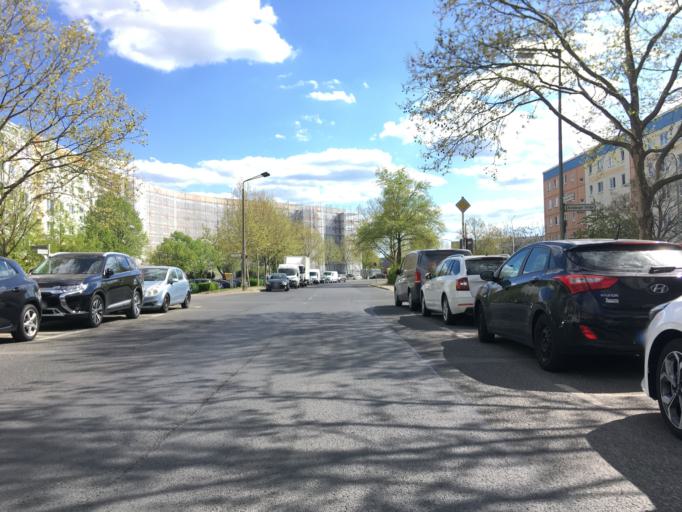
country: DE
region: Berlin
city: Hellersdorf
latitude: 52.5352
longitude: 13.6228
